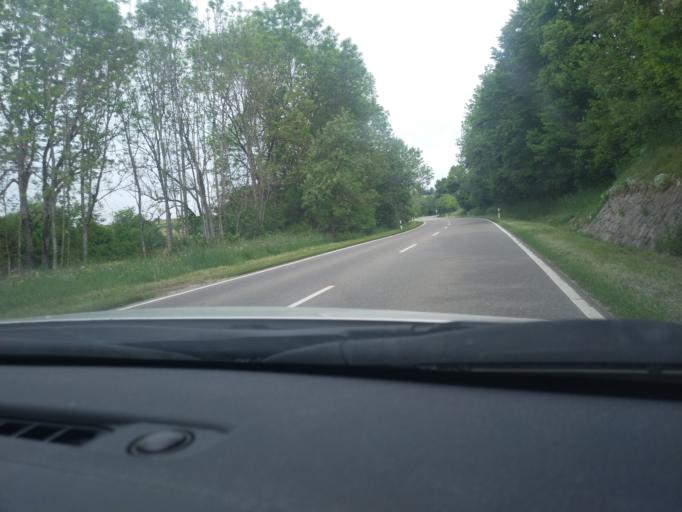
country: DE
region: Baden-Wuerttemberg
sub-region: Freiburg Region
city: Bonndorf im Schwarzwald
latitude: 47.8002
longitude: 8.3493
